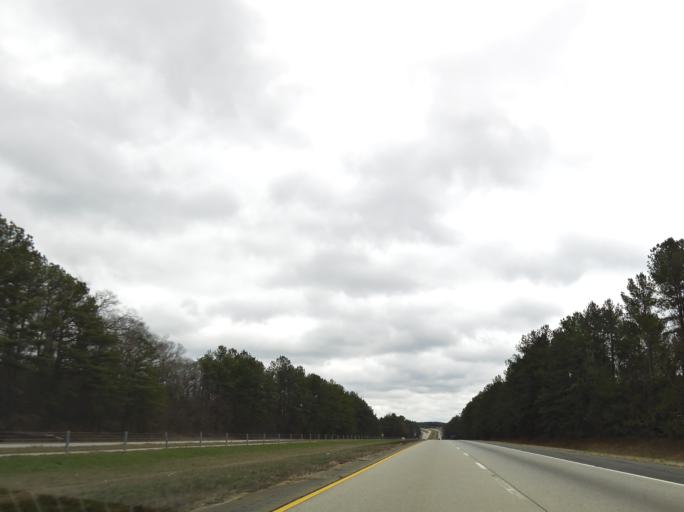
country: US
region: Georgia
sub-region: Houston County
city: Warner Robins
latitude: 32.7335
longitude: -83.5397
